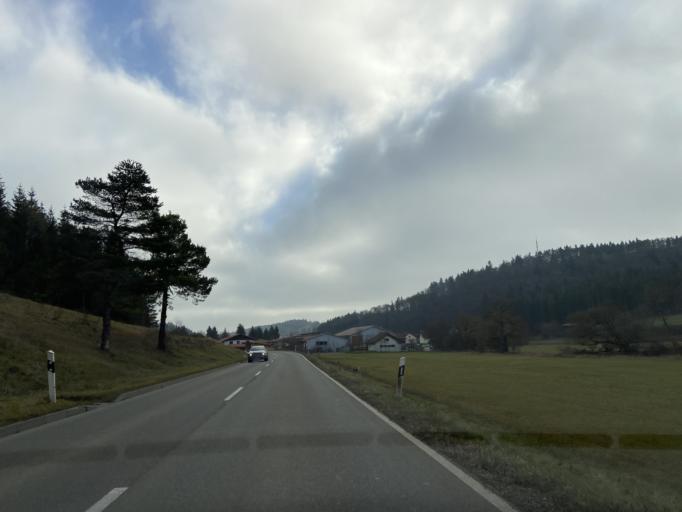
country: DE
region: Baden-Wuerttemberg
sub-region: Tuebingen Region
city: Neufra
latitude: 48.2562
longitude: 9.1750
